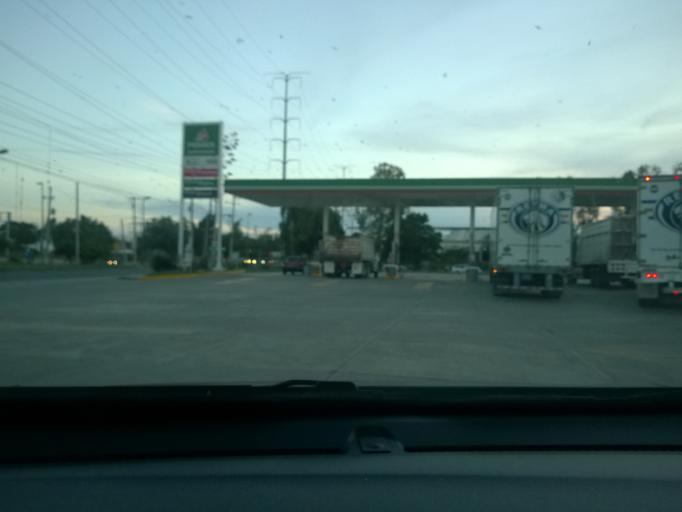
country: MX
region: Guanajuato
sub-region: Leon
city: San Jose de Duran (Los Troncoso)
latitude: 21.0687
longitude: -101.6843
